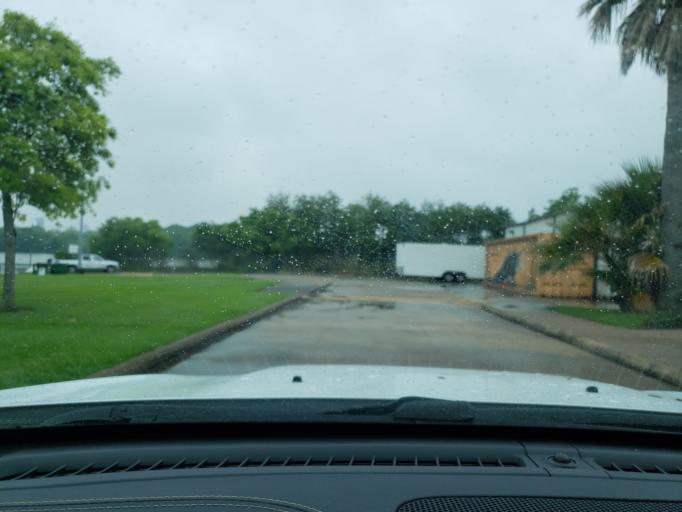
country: US
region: Texas
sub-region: Harris County
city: Baytown
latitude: 29.7328
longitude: -94.9850
